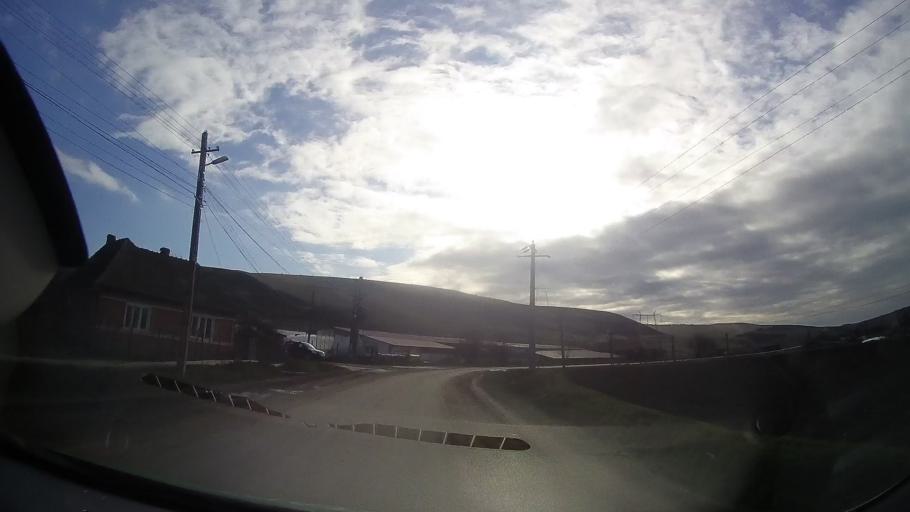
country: RO
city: Barza
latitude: 46.5499
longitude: 24.1289
